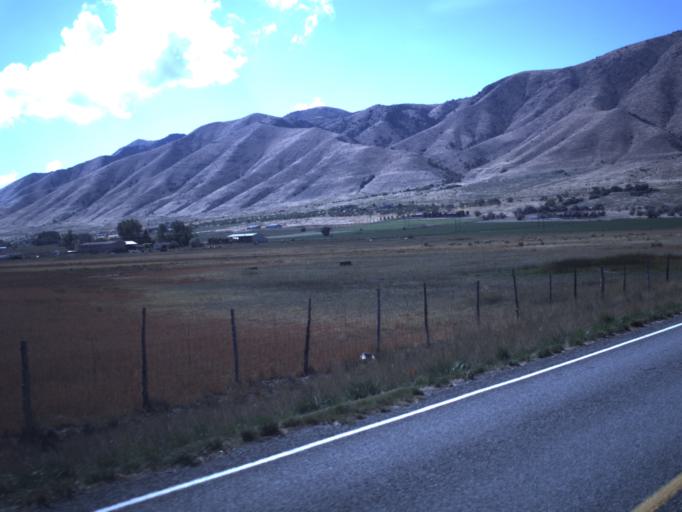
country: US
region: Utah
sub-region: Utah County
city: West Mountain
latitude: 40.0979
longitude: -111.7819
